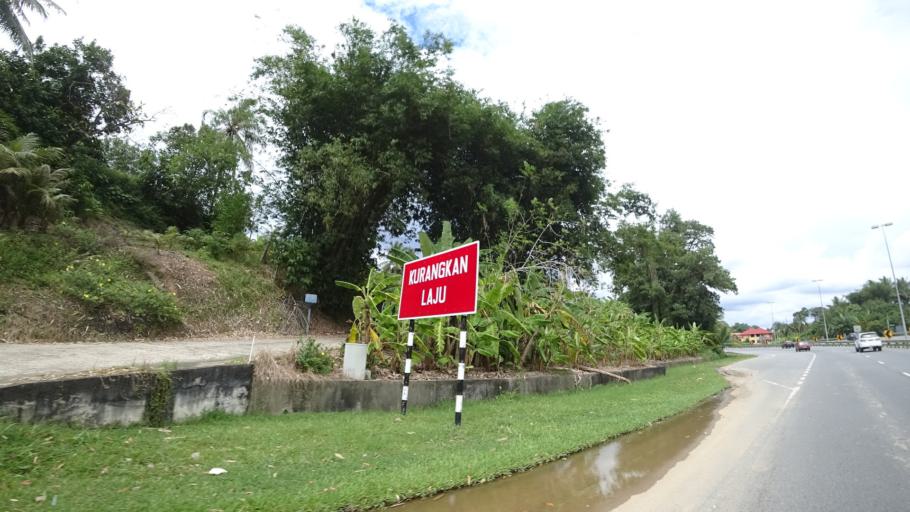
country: BN
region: Brunei and Muara
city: Bandar Seri Begawan
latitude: 4.8797
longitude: 114.8722
